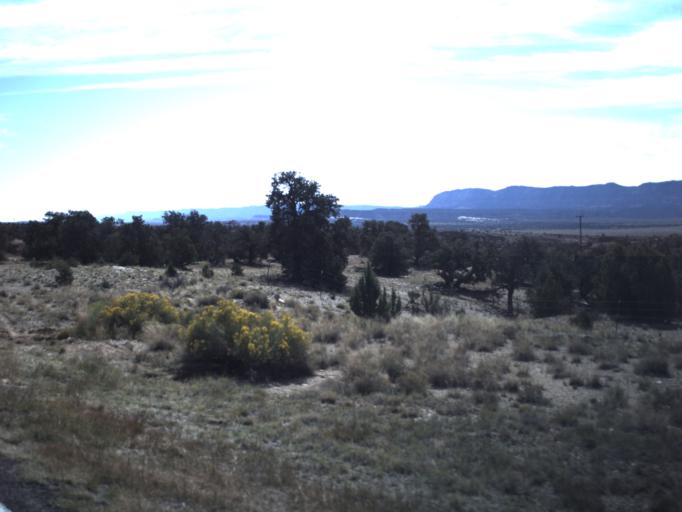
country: US
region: Utah
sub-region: Wayne County
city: Loa
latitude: 37.7381
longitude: -111.5480
